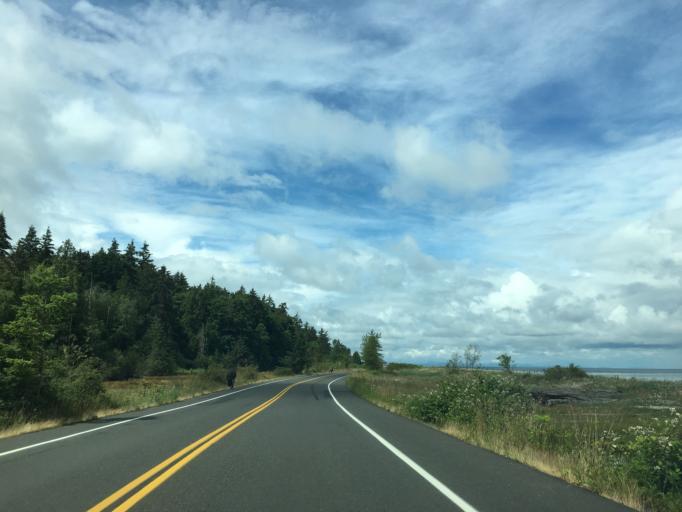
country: US
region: Washington
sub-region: Whatcom County
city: Birch Bay
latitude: 48.9078
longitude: -122.7578
